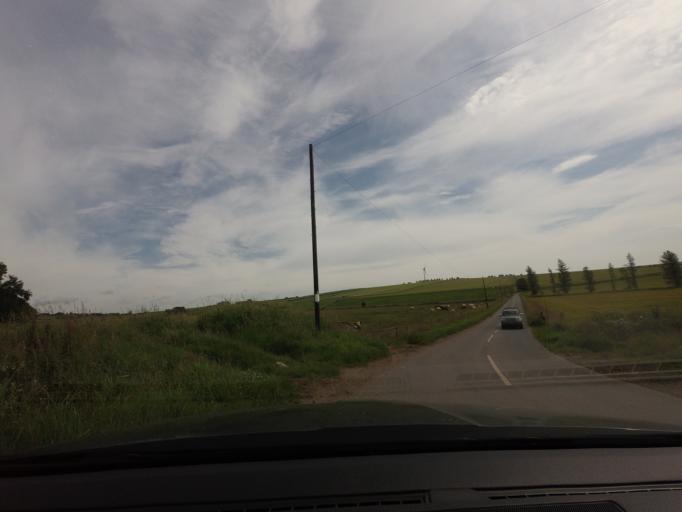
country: GB
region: Scotland
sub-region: Aberdeenshire
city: Turriff
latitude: 57.5591
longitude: -2.3125
